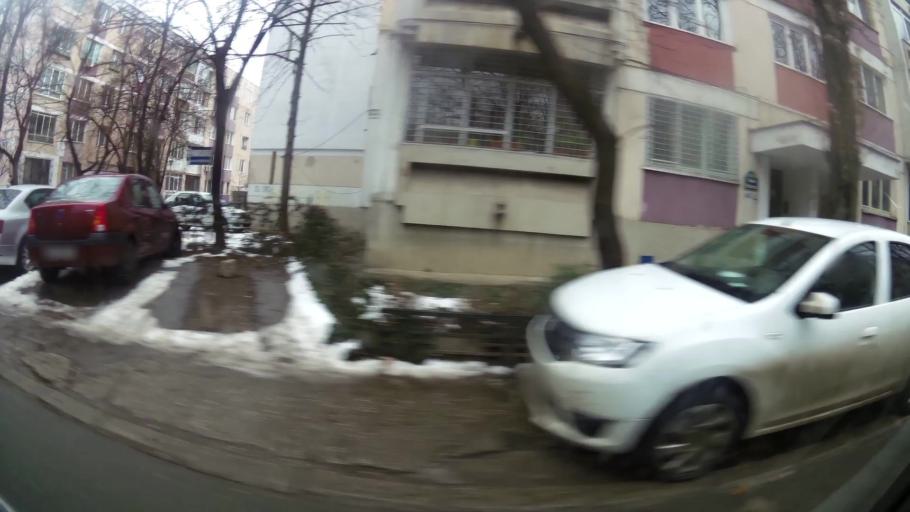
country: RO
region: Ilfov
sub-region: Comuna Chiajna
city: Rosu
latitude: 44.4365
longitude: 26.0423
